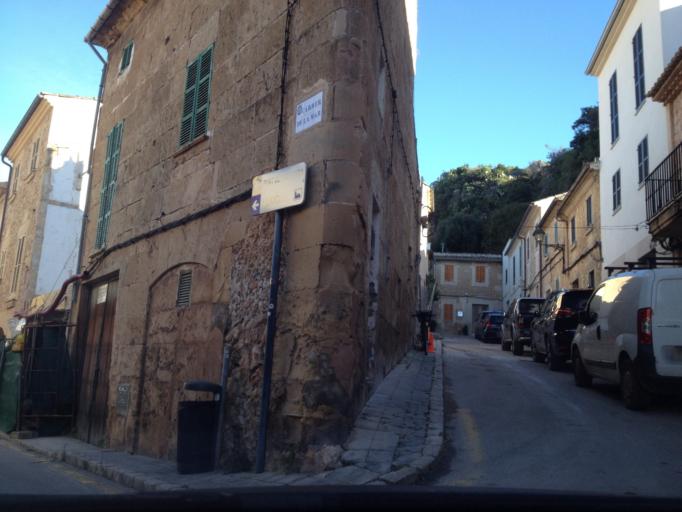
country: ES
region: Balearic Islands
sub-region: Illes Balears
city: Pollenca
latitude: 39.8799
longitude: 3.0190
